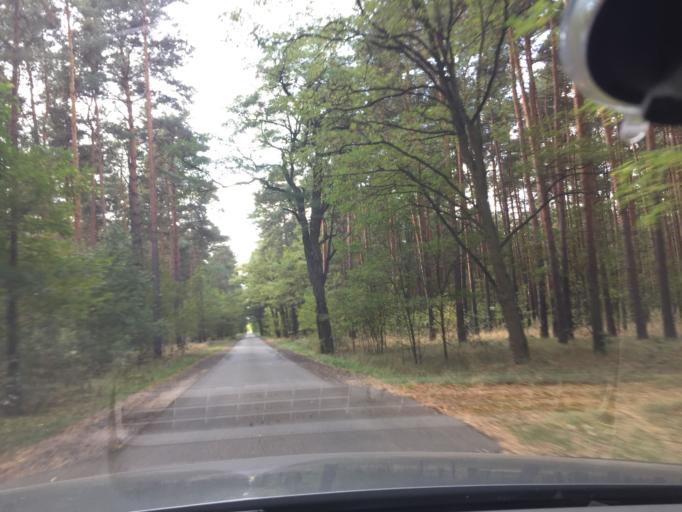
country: DE
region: Brandenburg
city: Spreenhagen
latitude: 52.3695
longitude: 13.8871
